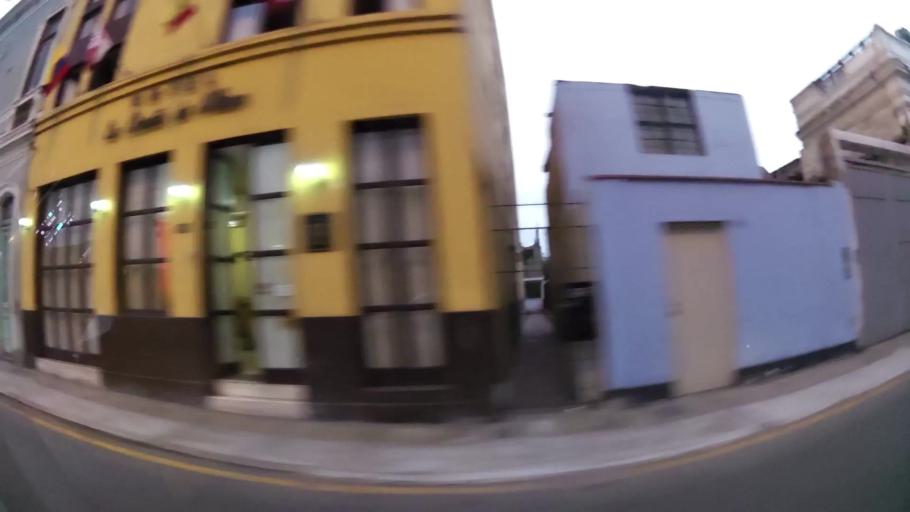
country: PE
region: Lima
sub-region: Lima
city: Surco
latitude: -12.1509
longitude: -77.0216
